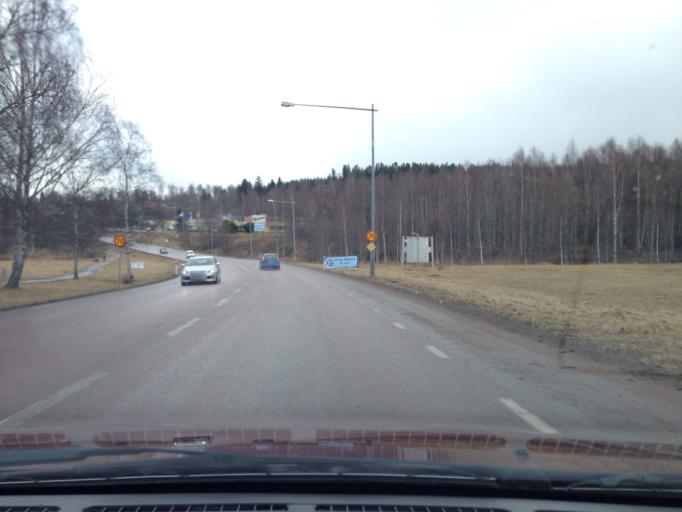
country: SE
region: Dalarna
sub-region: Ludvika Kommun
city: Ludvika
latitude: 60.1488
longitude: 15.2128
